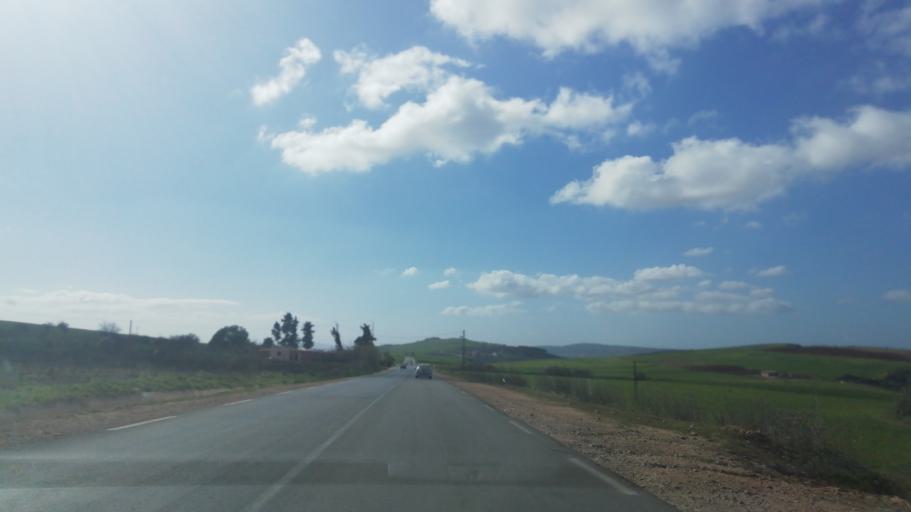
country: DZ
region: Relizane
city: Relizane
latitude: 36.0934
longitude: 0.4577
